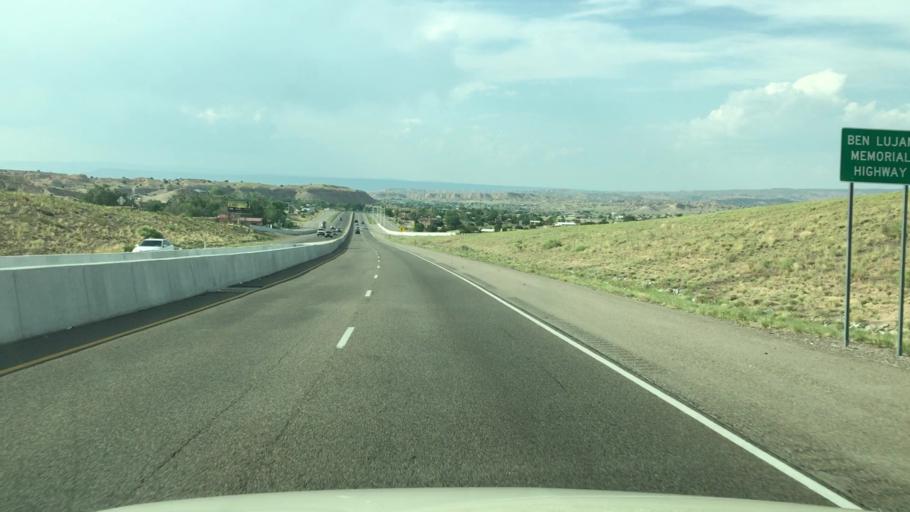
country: US
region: New Mexico
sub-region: Santa Fe County
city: El Valle de Arroyo Seco
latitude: 35.9289
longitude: -106.0176
